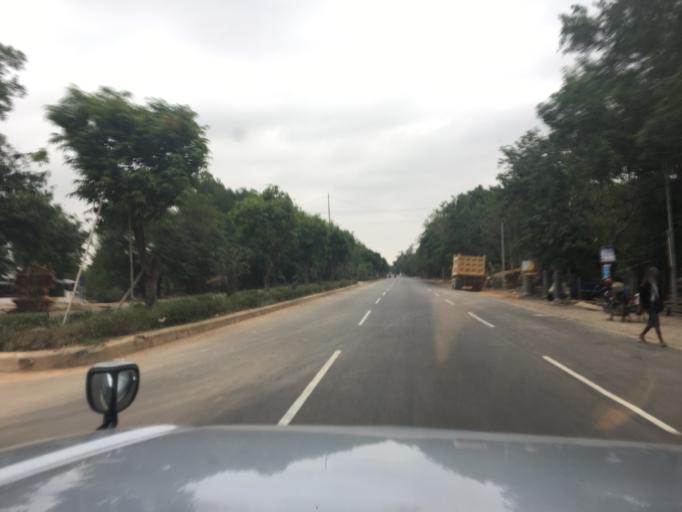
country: MM
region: Bago
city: Bago
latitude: 17.2252
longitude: 96.4493
